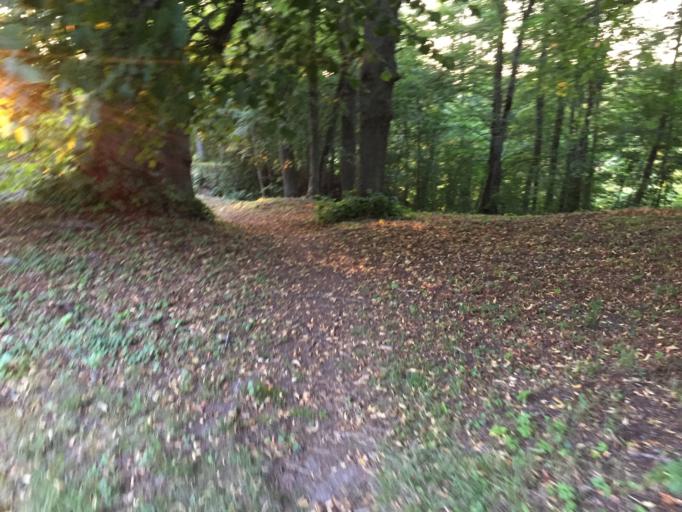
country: LV
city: Tervete
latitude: 56.4815
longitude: 23.3867
